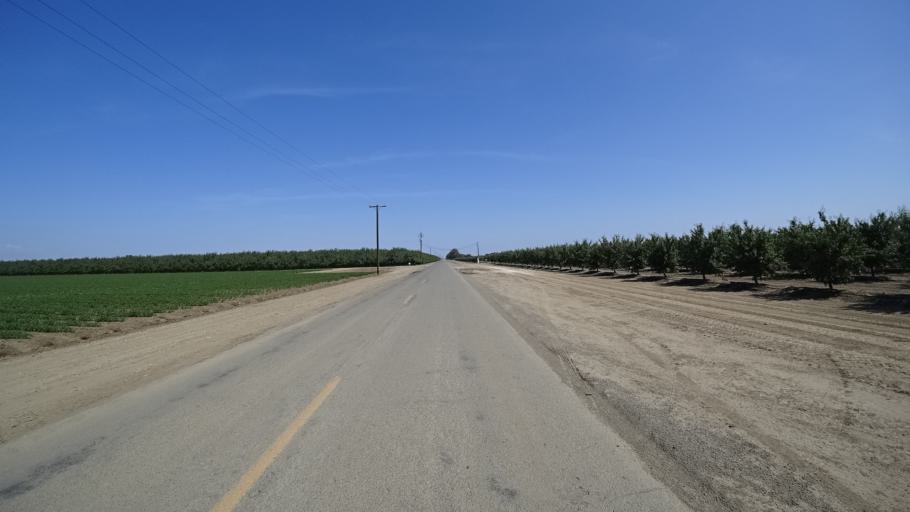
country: US
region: California
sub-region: Kings County
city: Kettleman City
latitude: 36.0857
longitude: -120.0037
